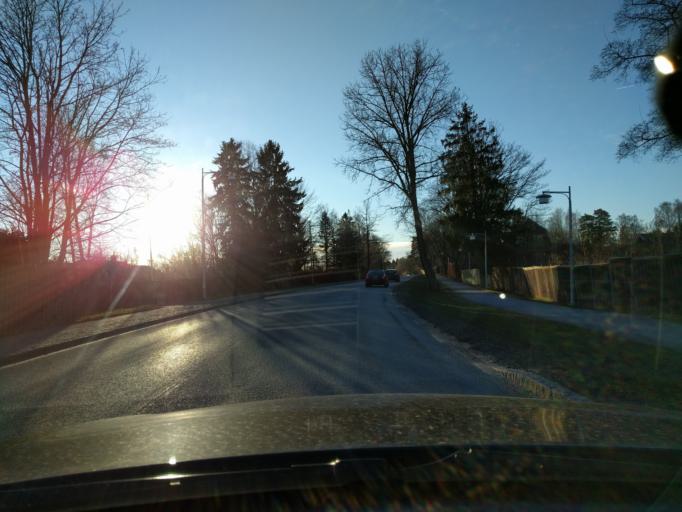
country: SE
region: Stockholm
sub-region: Taby Kommun
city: Taby
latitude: 59.4883
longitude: 18.0577
